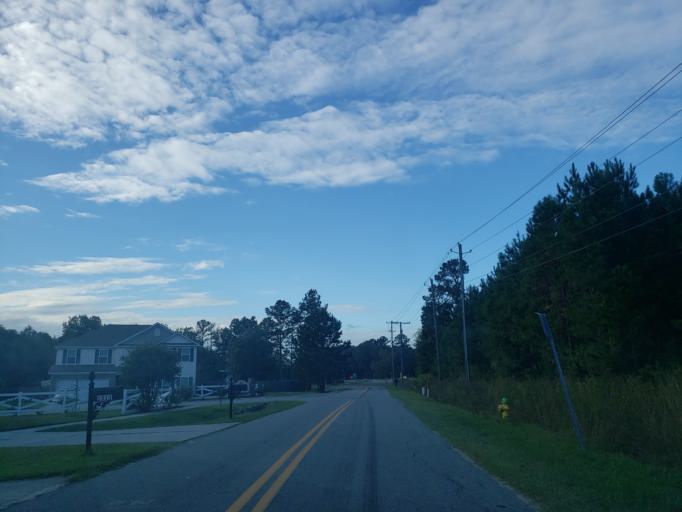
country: US
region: Georgia
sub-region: Chatham County
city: Georgetown
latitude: 31.9967
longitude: -81.2432
